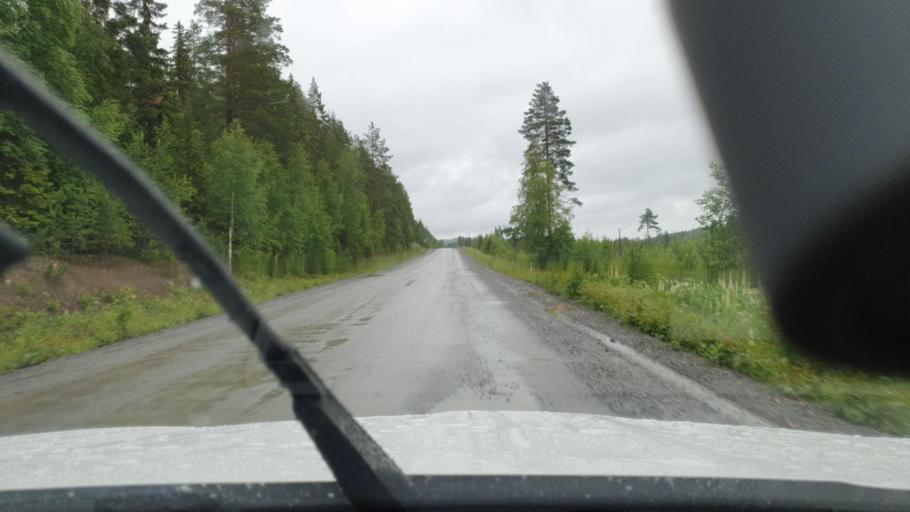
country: SE
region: Vaesterbotten
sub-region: Skelleftea Kommun
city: Burtraesk
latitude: 64.3750
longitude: 20.3616
